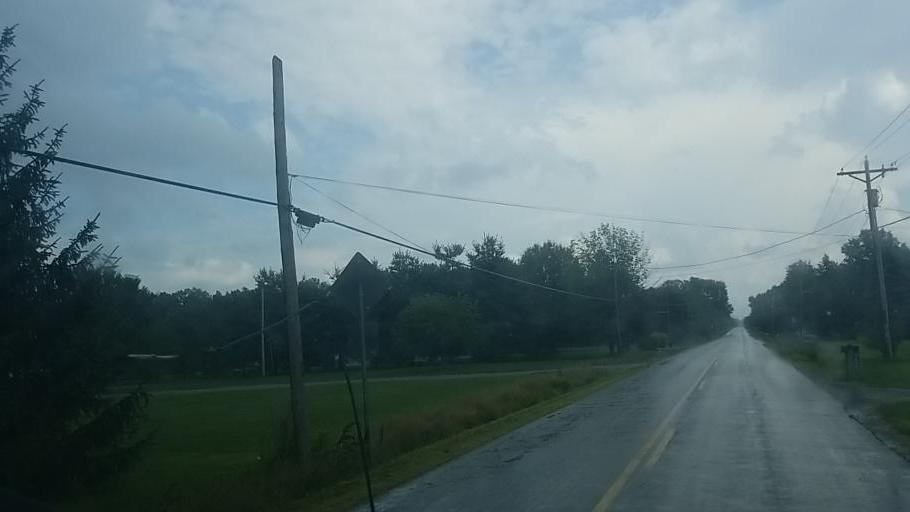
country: US
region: Ohio
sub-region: Lorain County
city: Grafton
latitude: 41.1850
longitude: -82.0368
